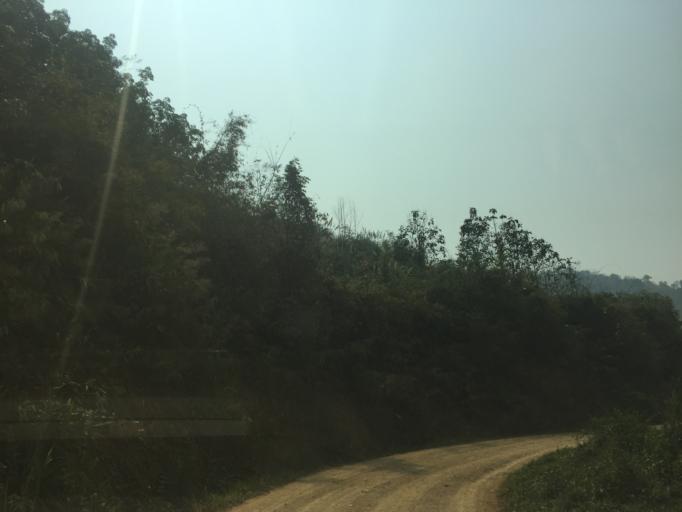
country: TH
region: Phayao
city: Phu Sang
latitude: 19.6267
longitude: 100.5365
